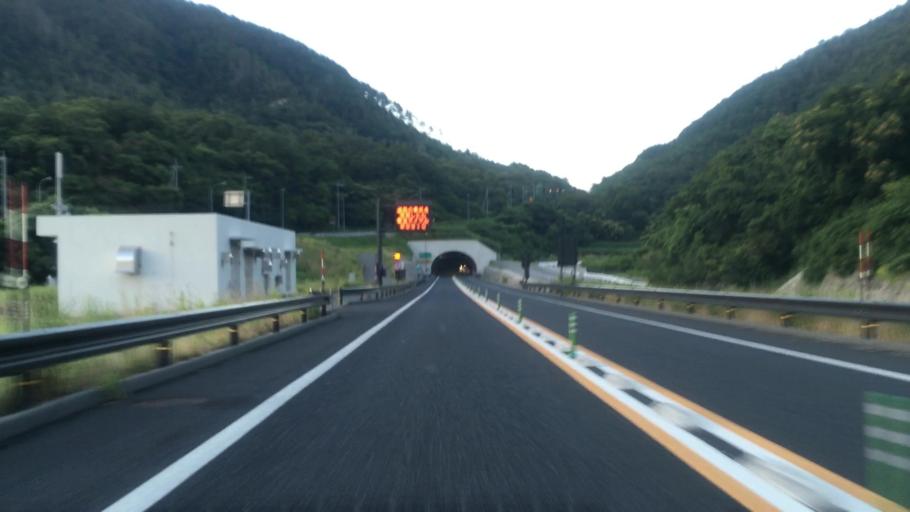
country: JP
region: Tottori
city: Tottori
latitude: 35.5593
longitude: 134.2837
